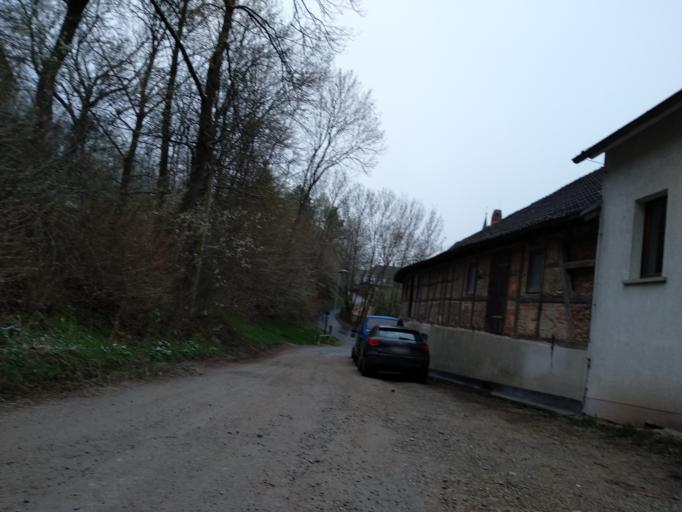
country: DE
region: Thuringia
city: Buchfart
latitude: 50.8924
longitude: 11.3262
